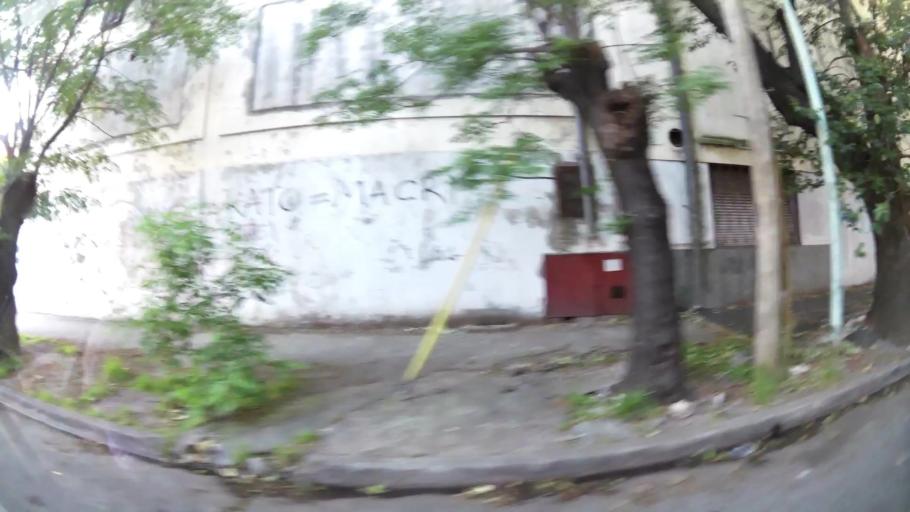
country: AR
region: Buenos Aires
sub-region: Partido de General San Martin
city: General San Martin
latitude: -34.5729
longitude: -58.5486
